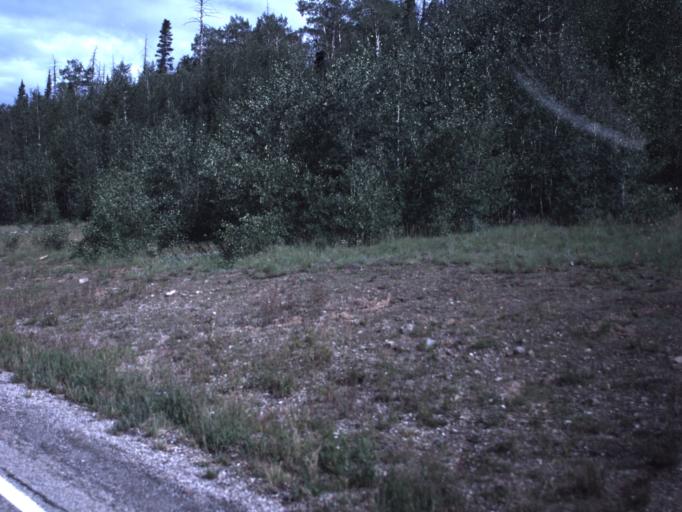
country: US
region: Utah
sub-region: Iron County
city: Cedar City
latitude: 37.5724
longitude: -112.8205
